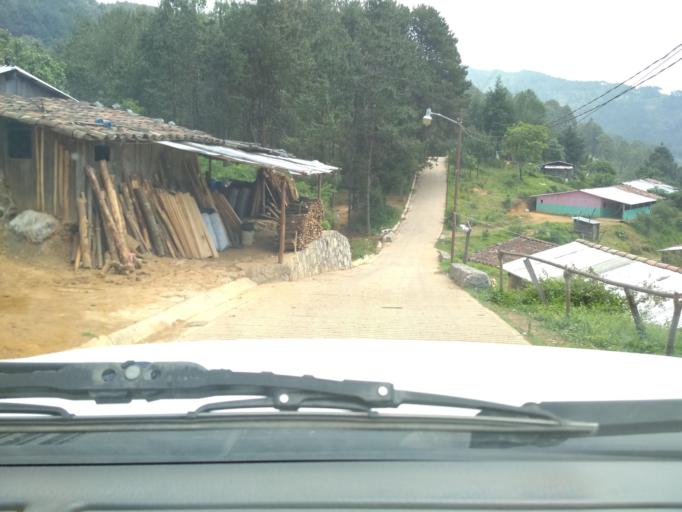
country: MX
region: Veracruz
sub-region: Camerino Z. Mendoza
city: Necoxtla
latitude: 18.7789
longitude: -97.1491
